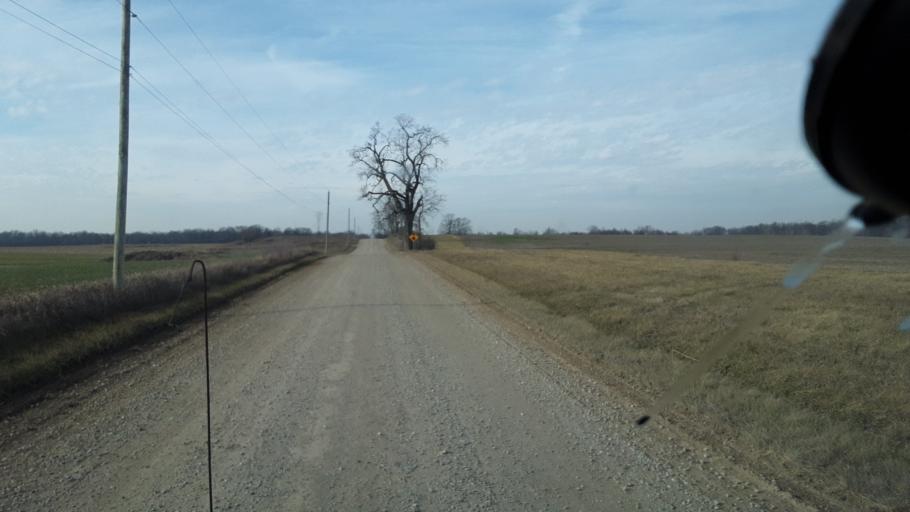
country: US
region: Indiana
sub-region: Allen County
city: Harlan
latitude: 41.2697
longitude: -84.8618
